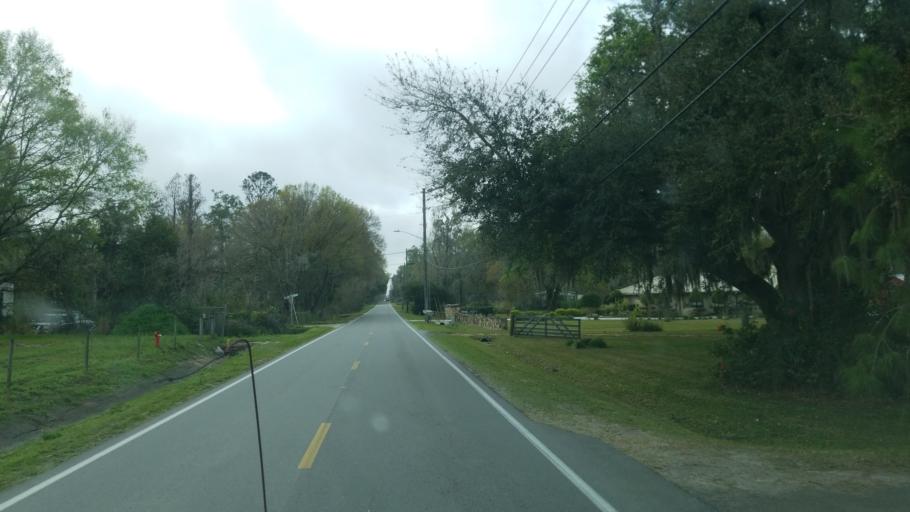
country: US
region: Florida
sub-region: Polk County
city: Kathleen
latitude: 28.1641
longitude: -82.0234
